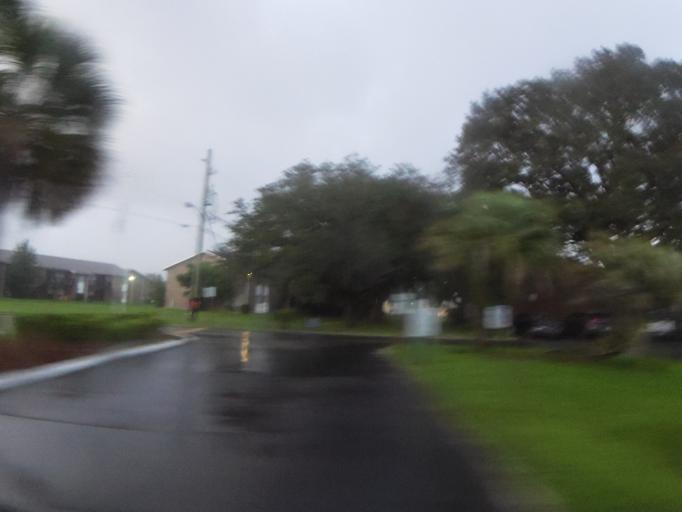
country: US
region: Florida
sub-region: Duval County
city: Jacksonville
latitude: 30.2481
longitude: -81.6206
